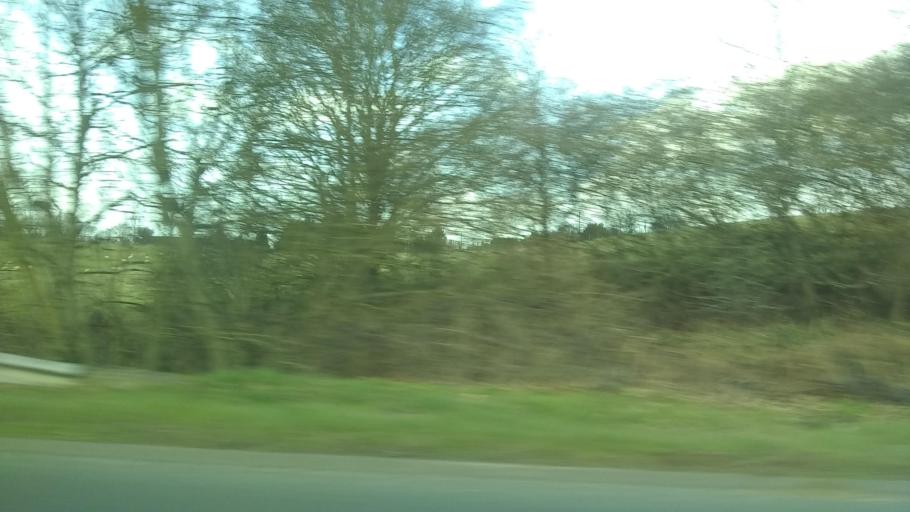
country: GB
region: England
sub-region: Worcestershire
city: Bewdley
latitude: 52.3664
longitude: -2.3131
